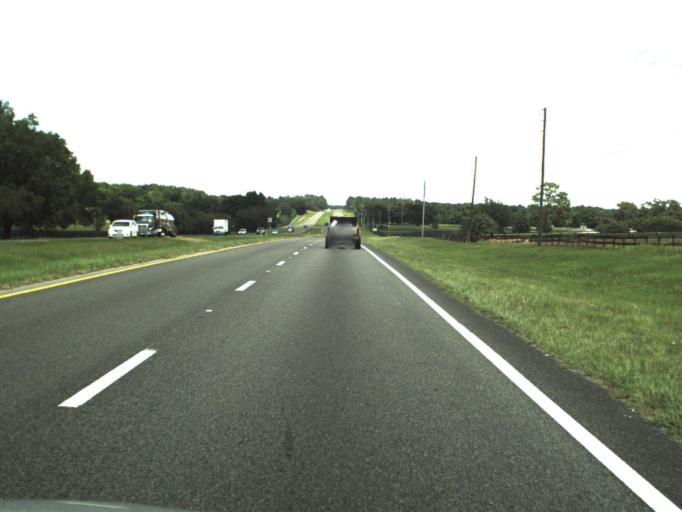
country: US
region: Florida
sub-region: Marion County
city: Citra
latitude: 29.3075
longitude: -82.1517
